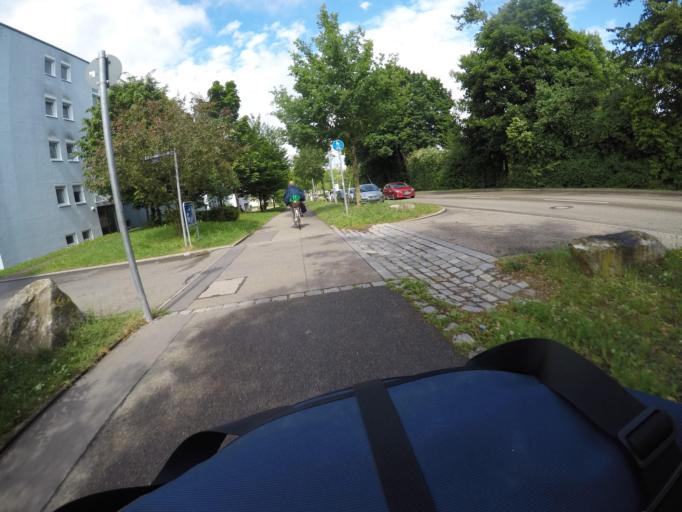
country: DE
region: Baden-Wuerttemberg
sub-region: Regierungsbezirk Stuttgart
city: Gerlingen
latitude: 48.7379
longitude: 9.0950
